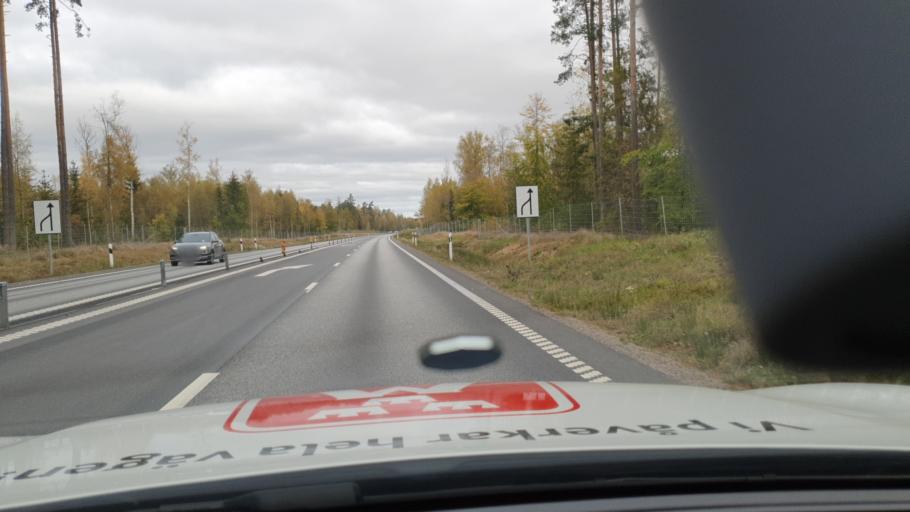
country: SE
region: OErebro
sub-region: Hallsbergs Kommun
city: Palsboda
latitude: 59.0891
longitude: 15.3076
